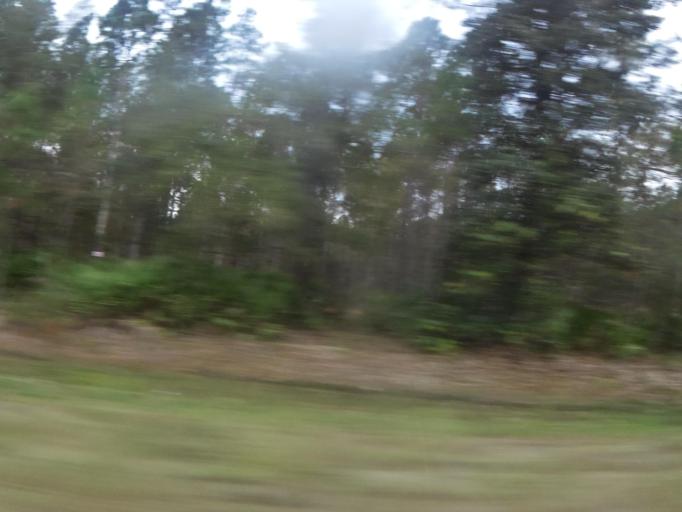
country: US
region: Georgia
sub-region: Charlton County
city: Folkston
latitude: 30.8741
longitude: -82.0264
